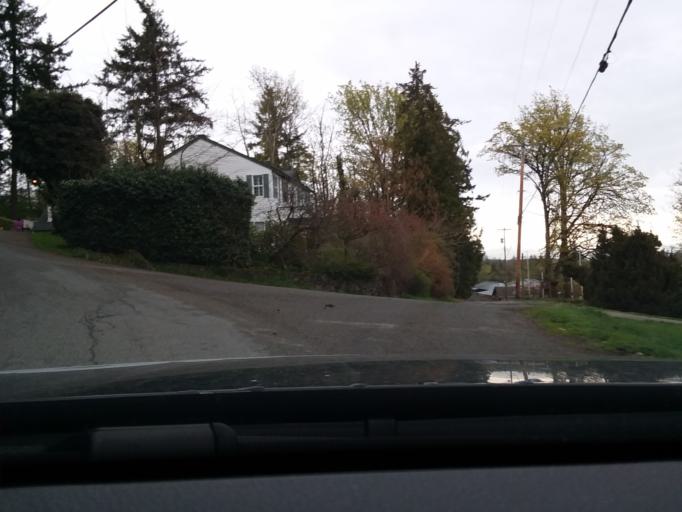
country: CA
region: British Columbia
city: North Saanich
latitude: 48.5539
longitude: -123.3900
